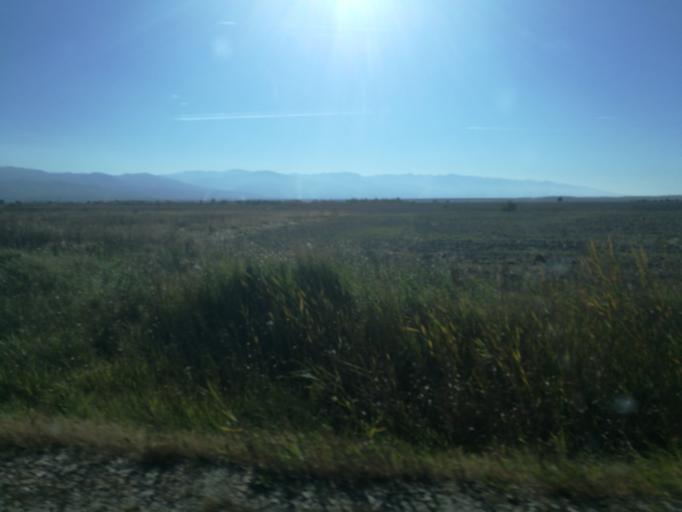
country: RO
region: Brasov
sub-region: Comuna Parau
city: Parau
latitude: 45.8094
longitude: 25.1700
